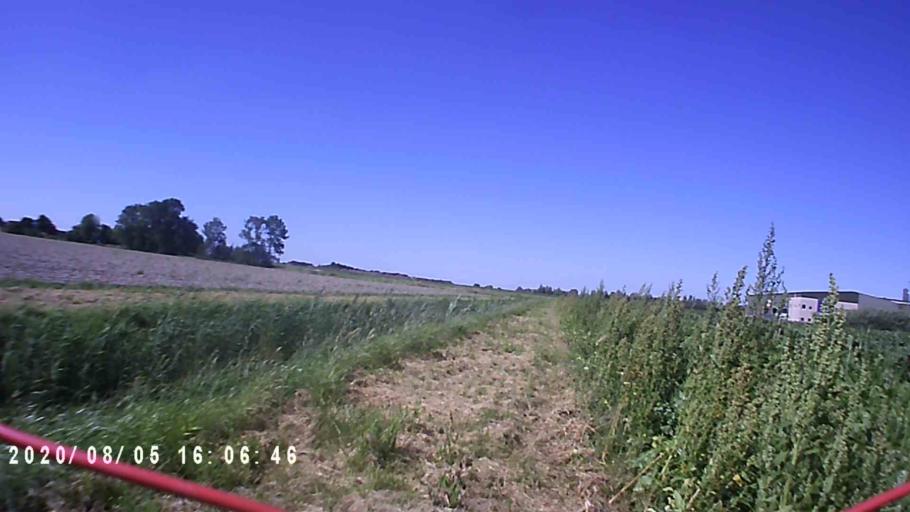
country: NL
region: Groningen
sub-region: Gemeente Winsum
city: Winsum
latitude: 53.3931
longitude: 6.5239
